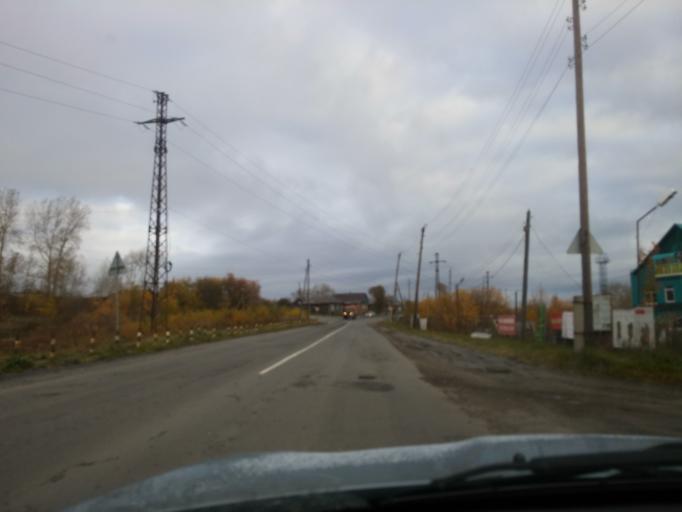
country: RU
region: Sverdlovsk
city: Turinsk
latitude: 58.0308
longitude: 63.7022
